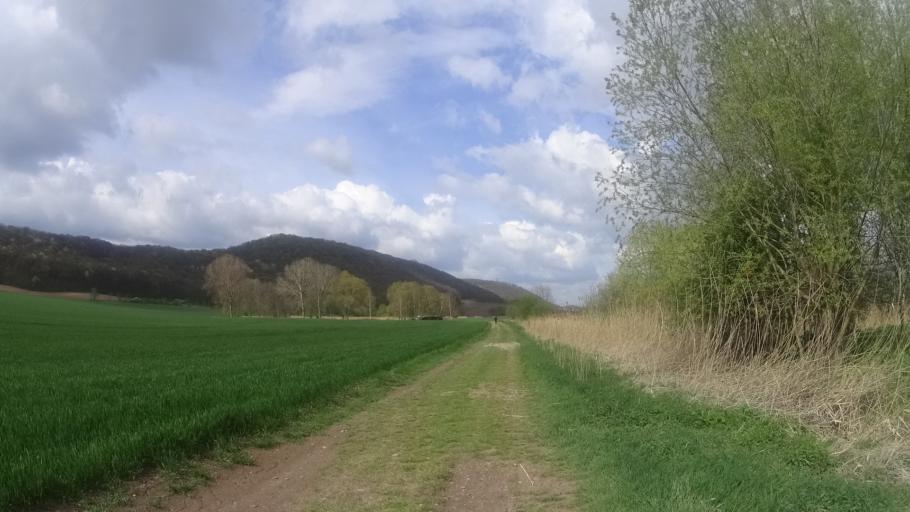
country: DE
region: Thuringia
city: Wandersleben
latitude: 50.8648
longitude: 10.8581
